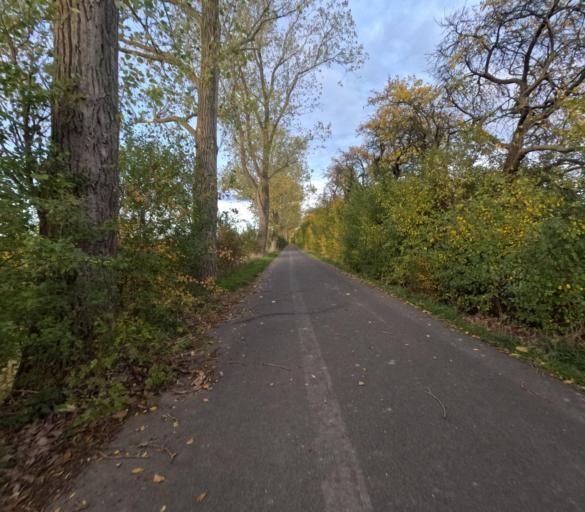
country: DE
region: Saxony
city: Grimma
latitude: 51.2442
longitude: 12.6926
